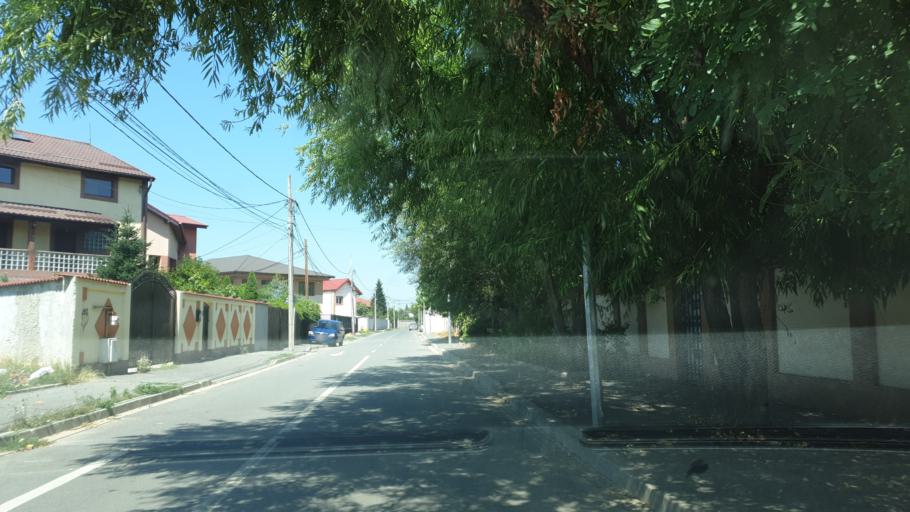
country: RO
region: Ilfov
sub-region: Comuna Chiajna
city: Rosu
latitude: 44.4649
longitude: 26.0212
